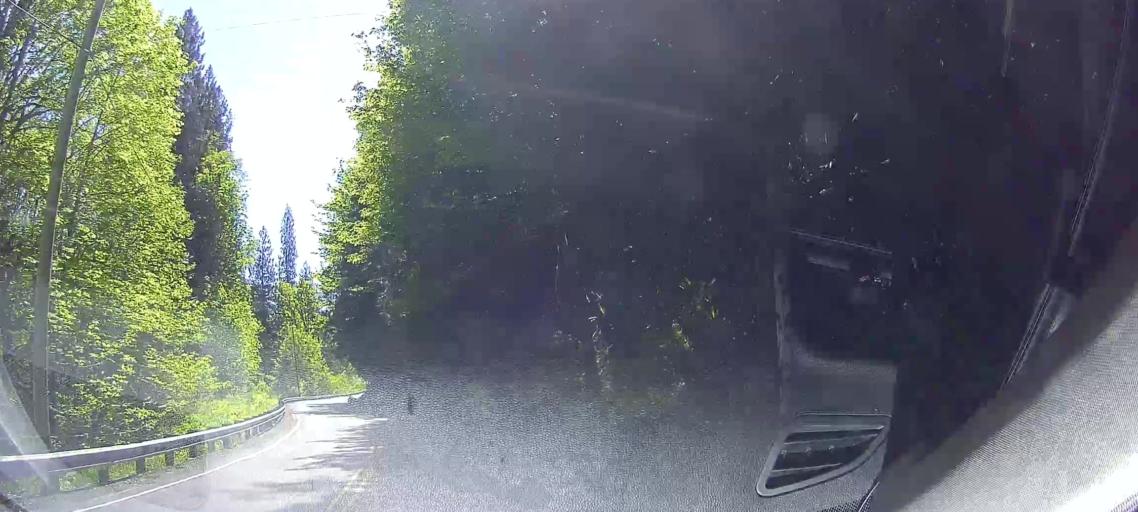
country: US
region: Washington
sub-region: Snohomish County
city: Darrington
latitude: 48.4763
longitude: -121.6467
